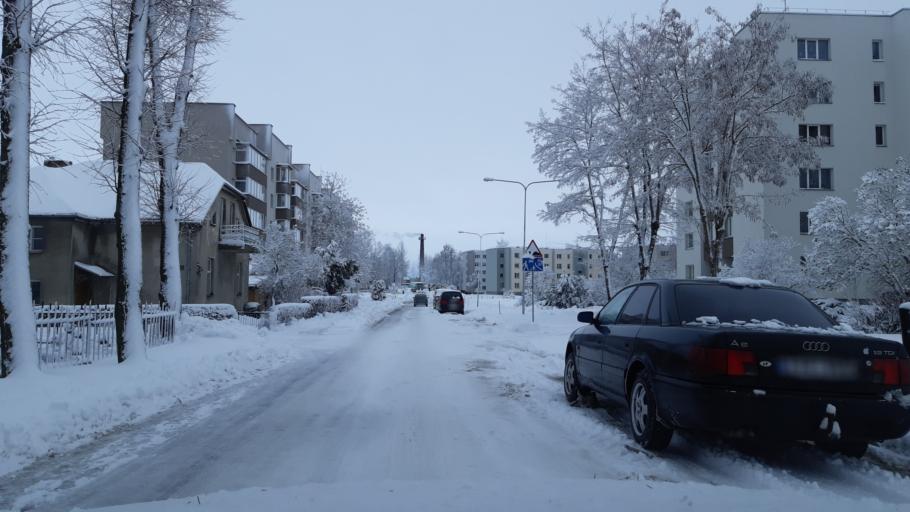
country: LT
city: Kybartai
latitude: 54.6368
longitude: 22.7566
